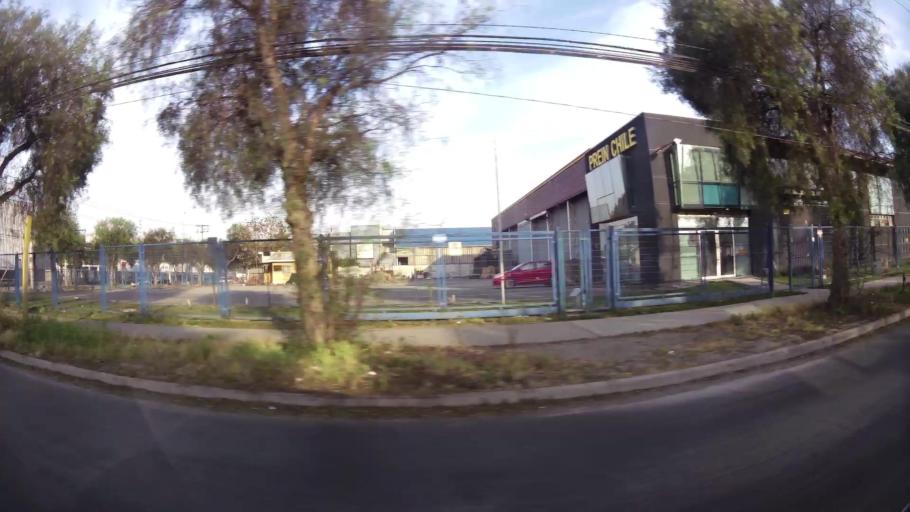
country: CL
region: Santiago Metropolitan
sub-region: Provincia de Maipo
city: San Bernardo
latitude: -33.5548
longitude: -70.7168
